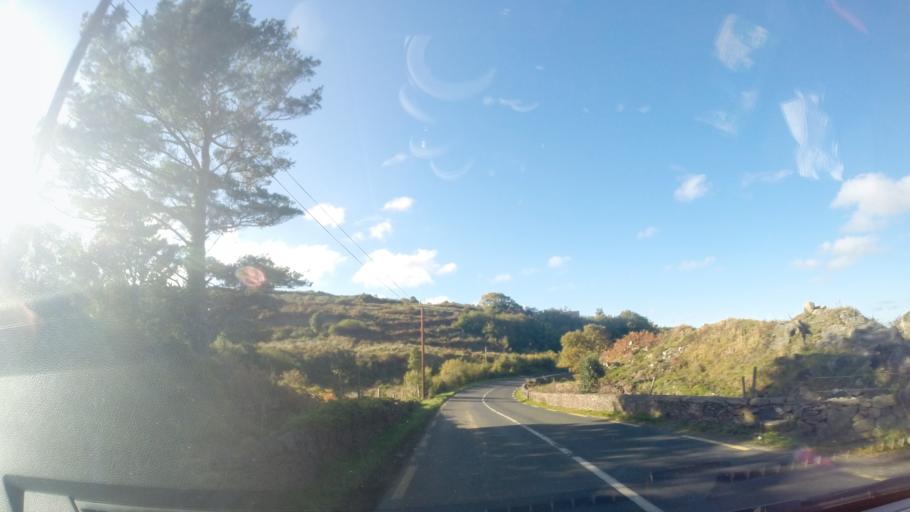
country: IE
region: Ulster
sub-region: County Donegal
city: Dungloe
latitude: 54.8339
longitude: -8.3525
